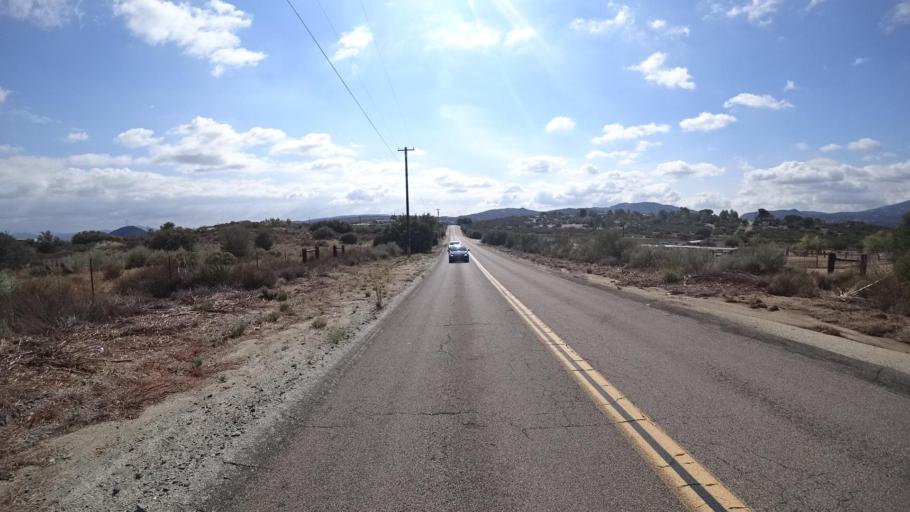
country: US
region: California
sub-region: San Diego County
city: Campo
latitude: 32.6875
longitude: -116.4936
